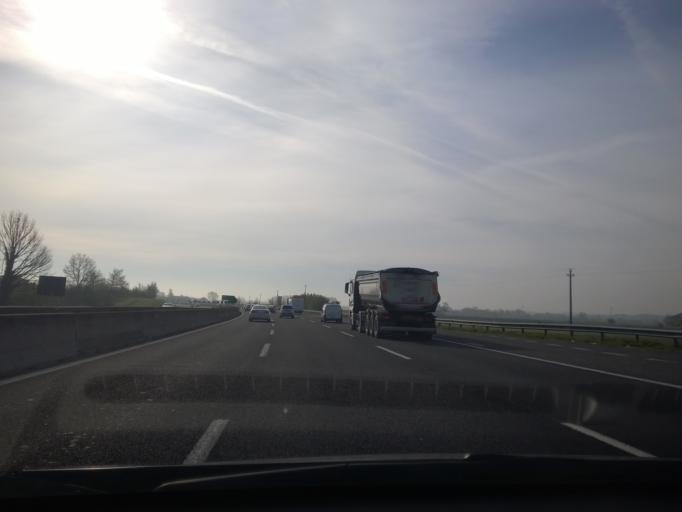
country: IT
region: Emilia-Romagna
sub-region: Provincia di Bologna
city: Toscanella
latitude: 44.4161
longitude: 11.6275
